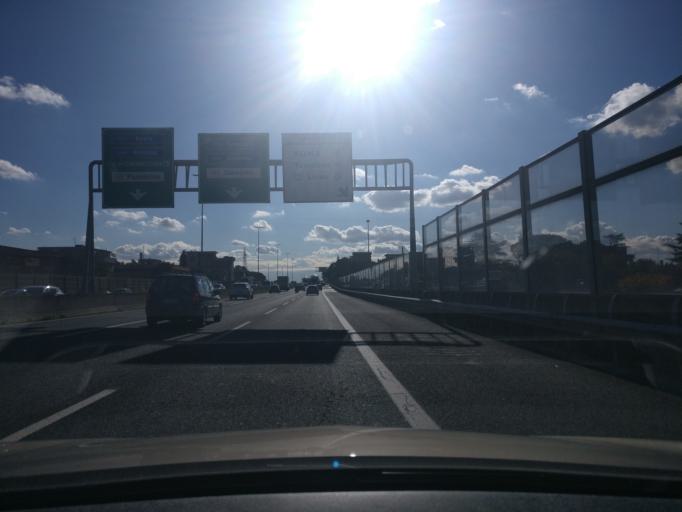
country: IT
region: Latium
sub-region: Citta metropolitana di Roma Capitale
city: Ciampino
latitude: 41.8437
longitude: 12.5935
